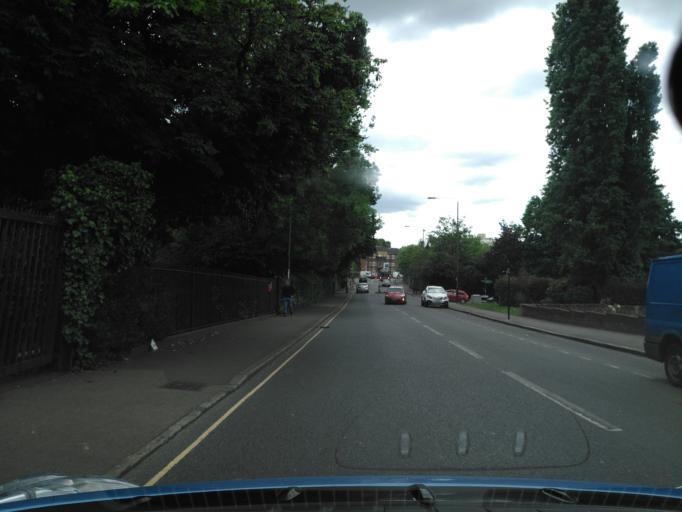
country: GB
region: England
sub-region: Greater London
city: Chislehurst
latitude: 51.4414
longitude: 0.0514
